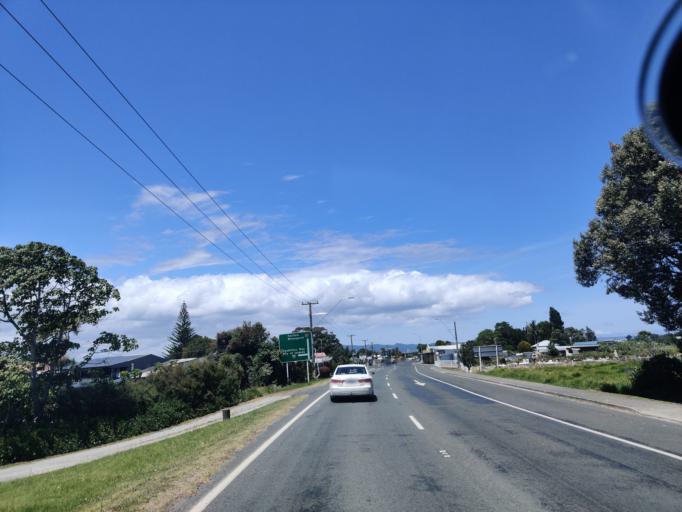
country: NZ
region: Northland
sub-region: Far North District
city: Kaitaia
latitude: -35.0447
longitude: 173.2567
